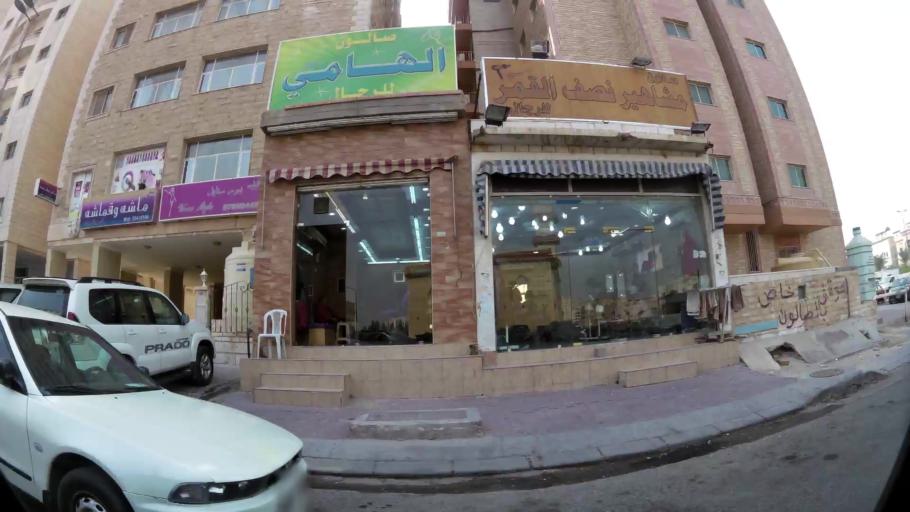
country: KW
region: Al Farwaniyah
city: Al Farwaniyah
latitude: 29.2822
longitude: 47.9516
